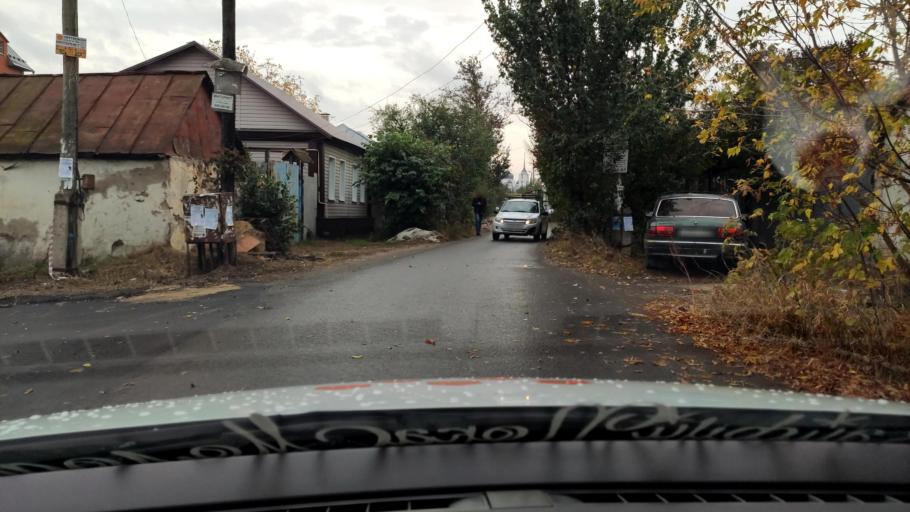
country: RU
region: Voronezj
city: Voronezh
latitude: 51.6859
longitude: 39.2077
